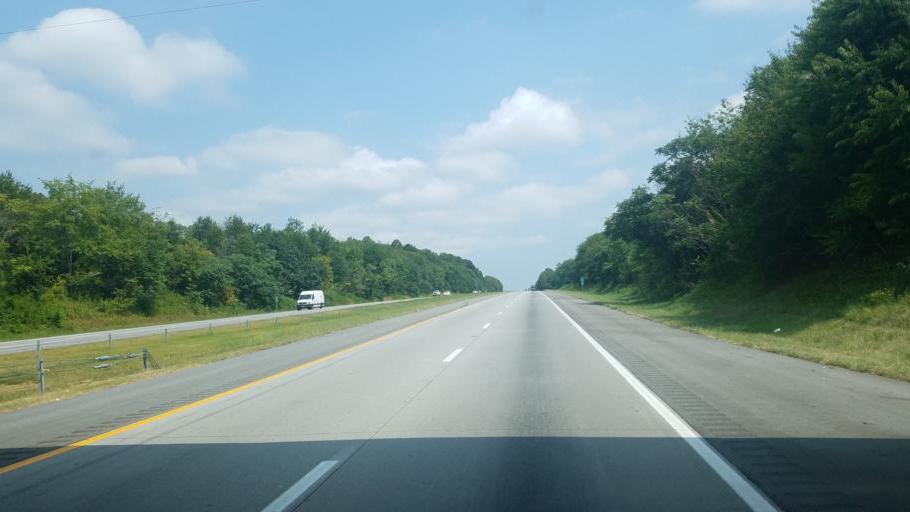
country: US
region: North Carolina
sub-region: Yadkin County
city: Jonesville
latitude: 36.1567
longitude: -80.8079
